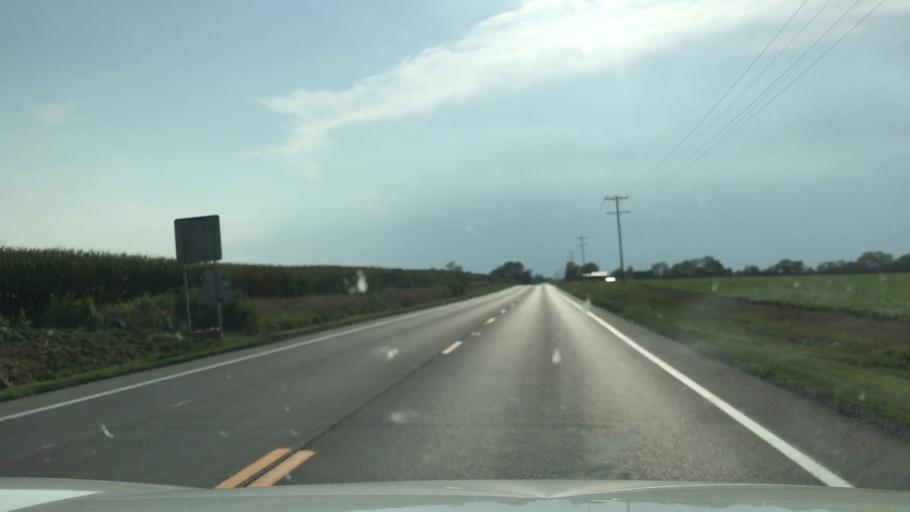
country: US
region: Illinois
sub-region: Washington County
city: Nashville
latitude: 38.4417
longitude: -89.3718
